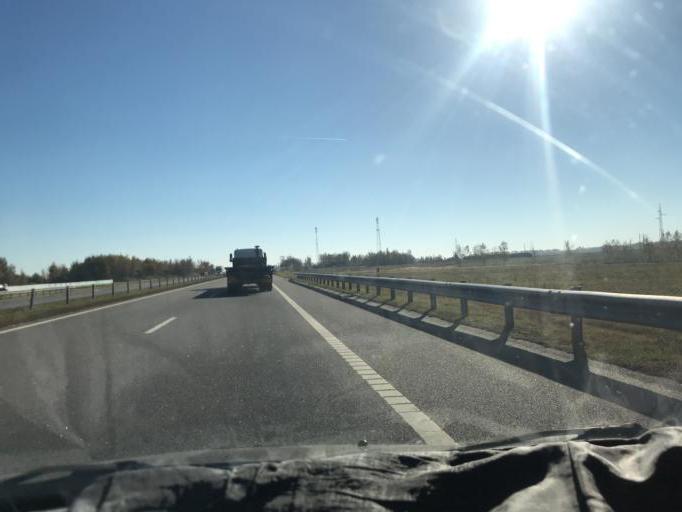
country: BY
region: Mogilev
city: Yalizava
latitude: 53.2518
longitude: 28.9211
